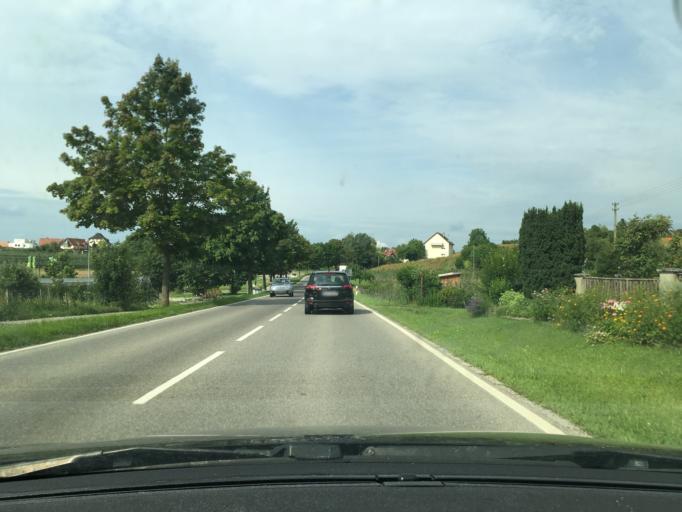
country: DE
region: Baden-Wuerttemberg
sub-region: Tuebingen Region
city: Stetten
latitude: 47.6936
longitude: 9.3051
